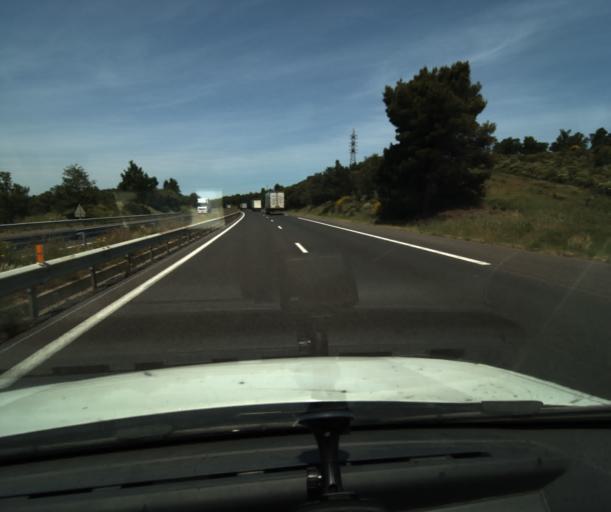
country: FR
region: Languedoc-Roussillon
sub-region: Departement des Pyrenees-Orientales
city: Banyuls-dels-Aspres
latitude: 42.5522
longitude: 2.8496
